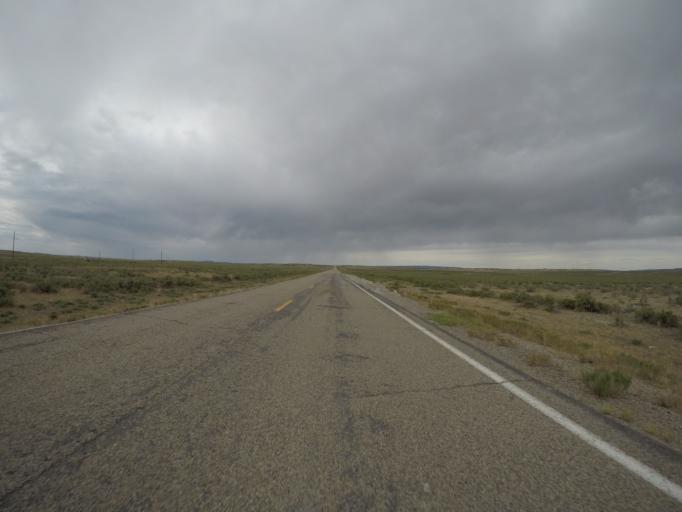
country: US
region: Wyoming
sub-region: Lincoln County
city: Kemmerer
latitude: 41.9635
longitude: -110.1402
